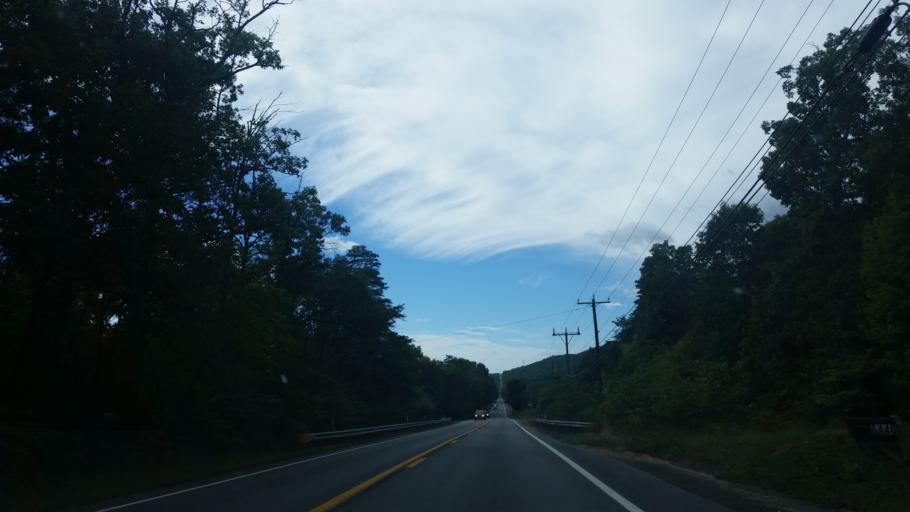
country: US
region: West Virginia
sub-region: Morgan County
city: Berkeley Springs
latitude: 39.5412
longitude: -78.2729
